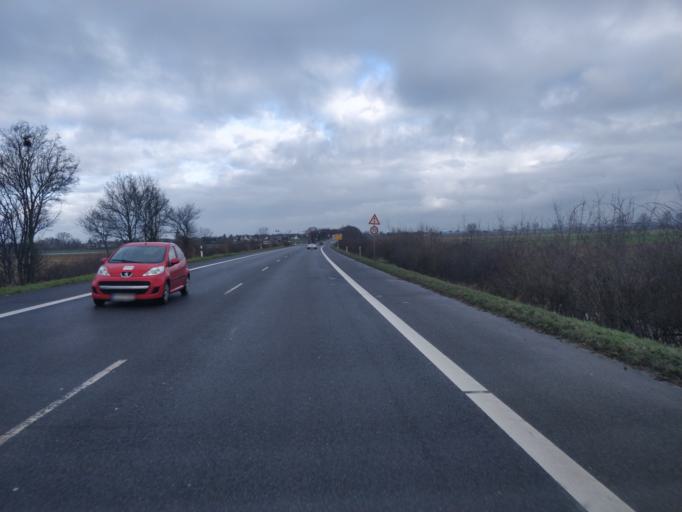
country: DE
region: North Rhine-Westphalia
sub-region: Regierungsbezirk Koln
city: Euskirchen
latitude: 50.6490
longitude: 6.8409
